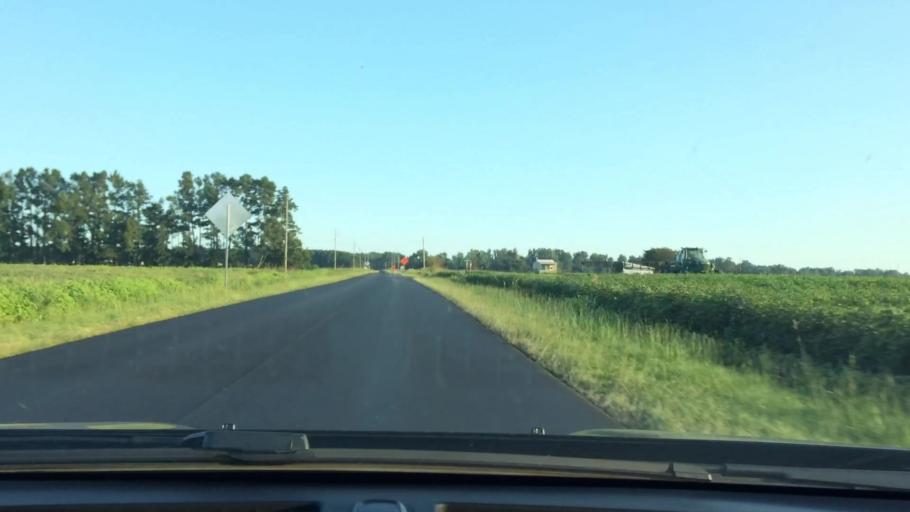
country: US
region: North Carolina
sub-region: Pitt County
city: Ayden
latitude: 35.4380
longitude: -77.4522
